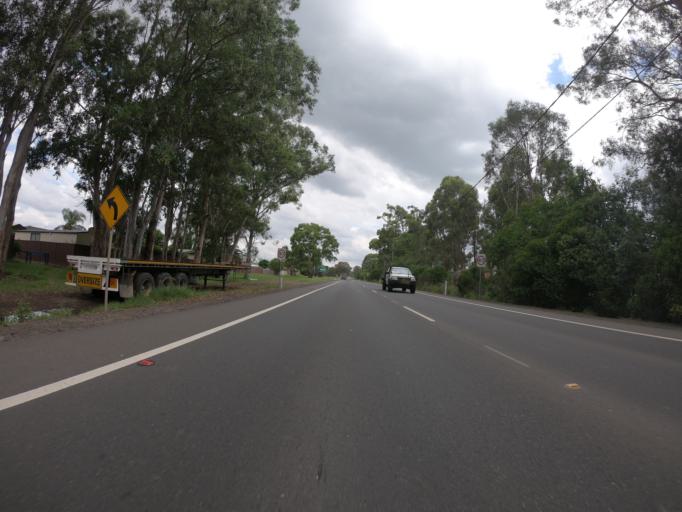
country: AU
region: New South Wales
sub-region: Blacktown
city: Mount Druitt
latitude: -33.7988
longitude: 150.7685
